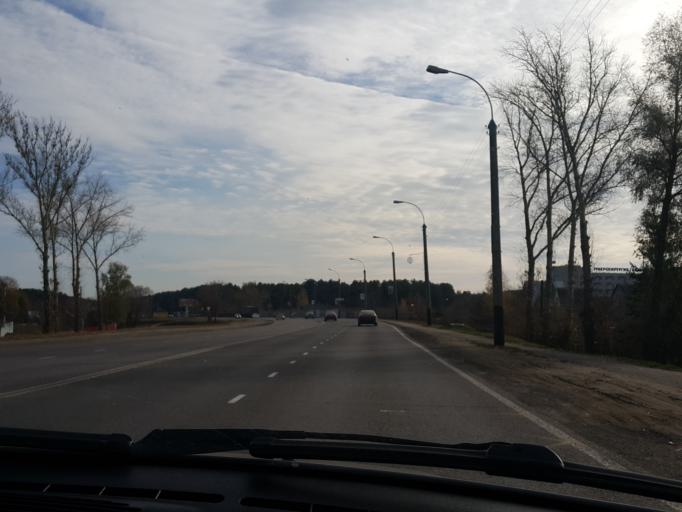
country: RU
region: Tambov
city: Tambov
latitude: 52.7173
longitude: 41.5043
